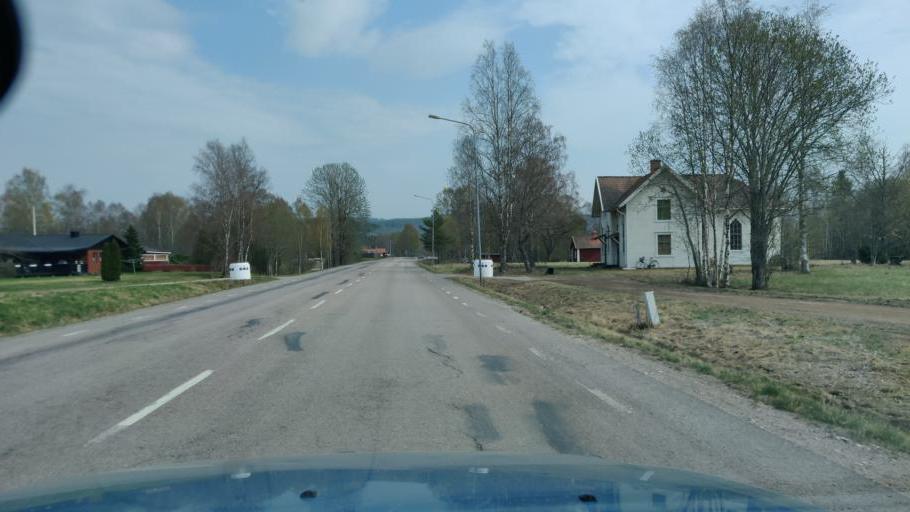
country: SE
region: Vaermland
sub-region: Munkfors Kommun
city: Munkfors
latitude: 59.8313
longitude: 13.5166
